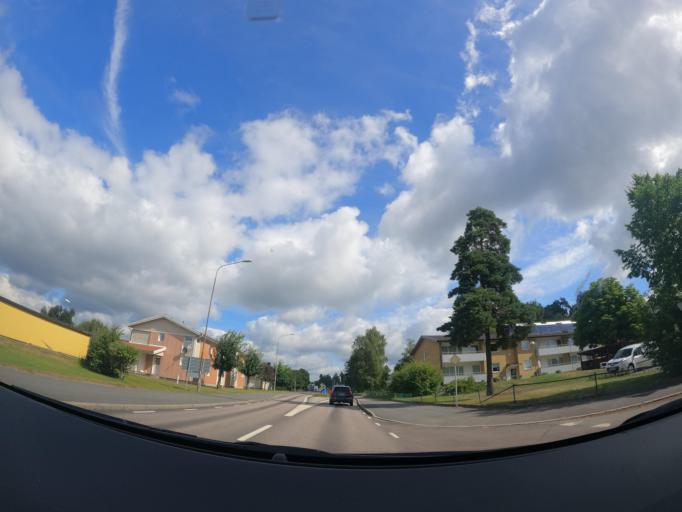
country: SE
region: Joenkoeping
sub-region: Gislaveds Kommun
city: Smalandsstenar
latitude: 57.1672
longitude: 13.4165
